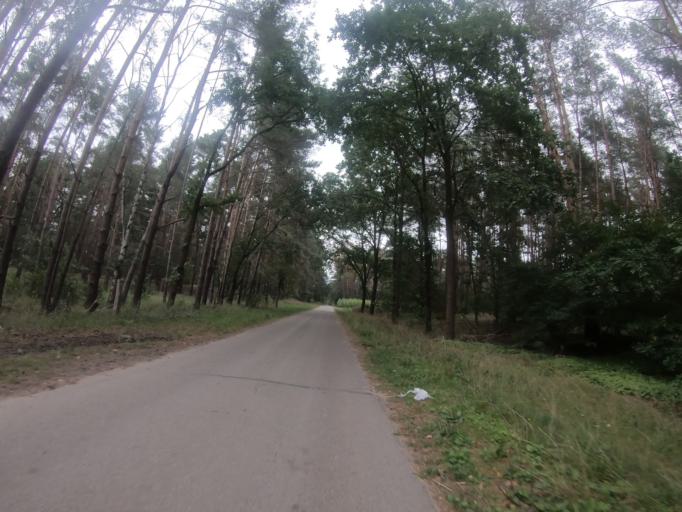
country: DE
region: Lower Saxony
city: Ribbesbuttel
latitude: 52.4443
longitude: 10.5181
